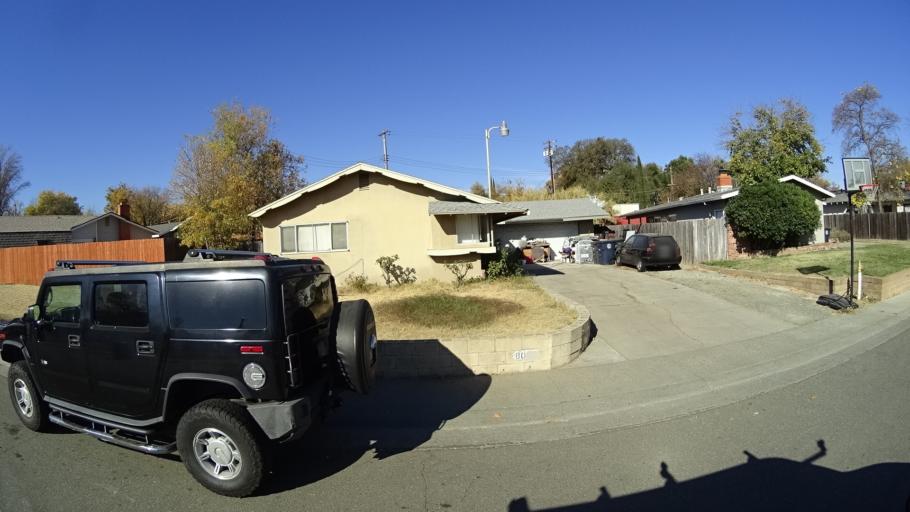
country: US
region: California
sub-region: Sacramento County
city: Antelope
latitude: 38.7120
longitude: -121.3066
